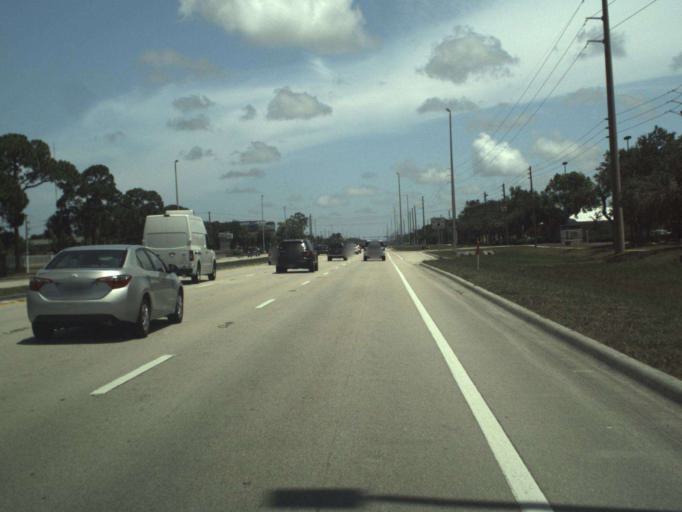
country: US
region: Florida
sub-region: Saint Lucie County
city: Port Saint Lucie
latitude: 27.2835
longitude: -80.2957
